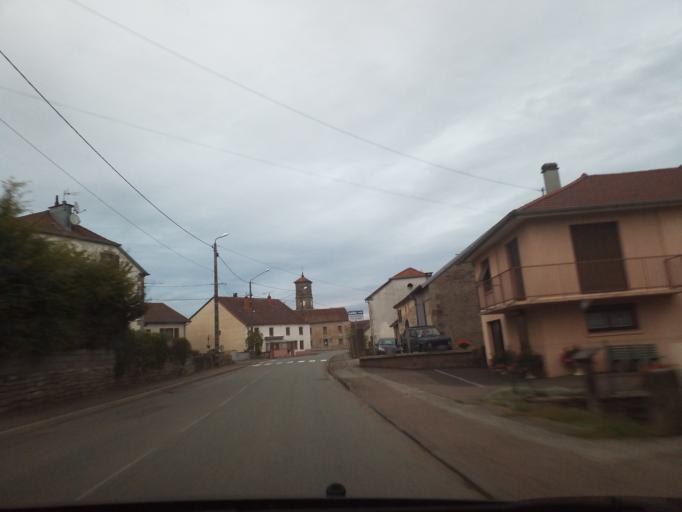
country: FR
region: Franche-Comte
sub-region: Departement de la Haute-Saone
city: Saint-Germain
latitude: 47.7212
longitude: 6.5289
